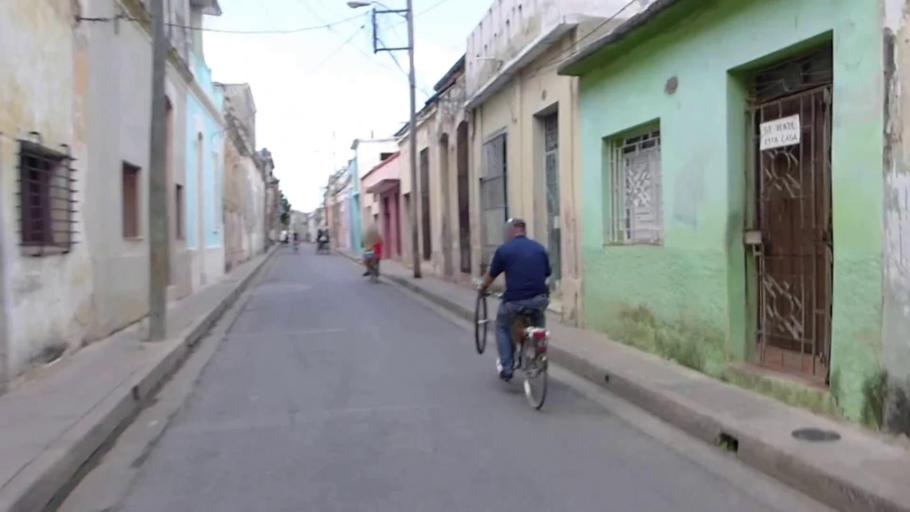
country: CU
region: Camaguey
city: Camaguey
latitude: 21.3868
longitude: -77.9173
